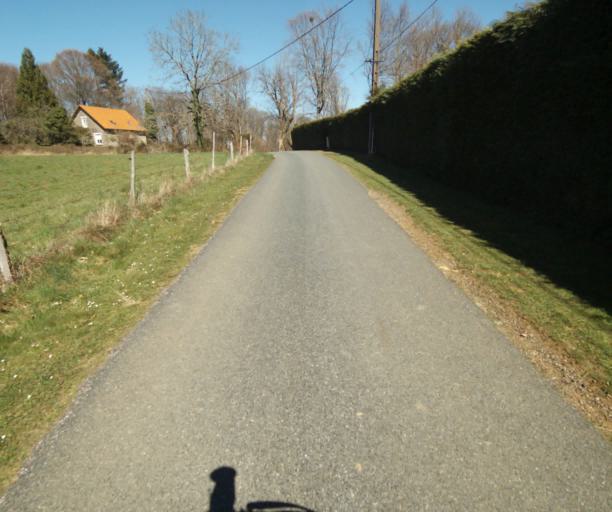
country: FR
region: Limousin
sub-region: Departement de la Correze
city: Uzerche
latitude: 45.3874
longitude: 1.6065
